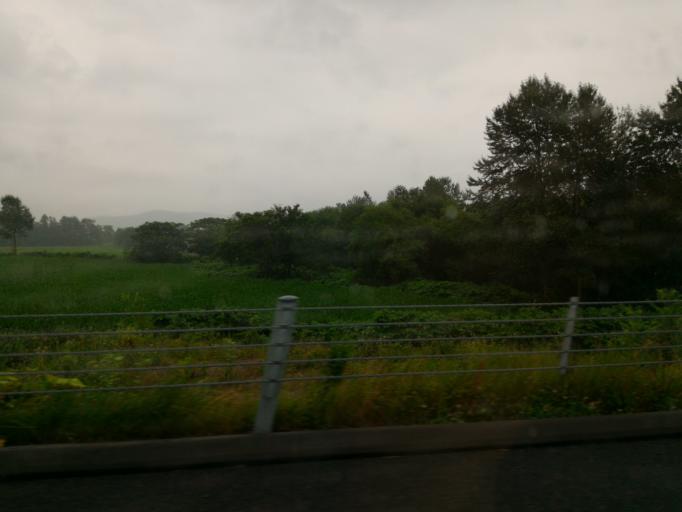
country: JP
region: Hokkaido
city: Nayoro
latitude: 44.4668
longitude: 142.3738
